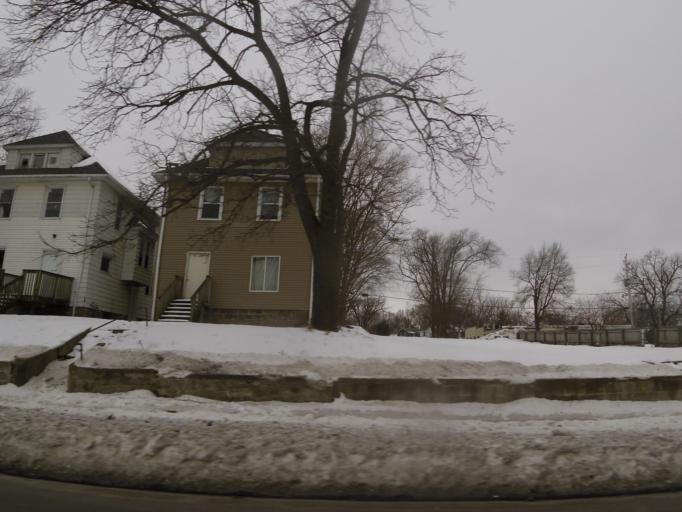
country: US
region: Iowa
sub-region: Black Hawk County
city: Waterloo
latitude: 42.4888
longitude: -92.3366
